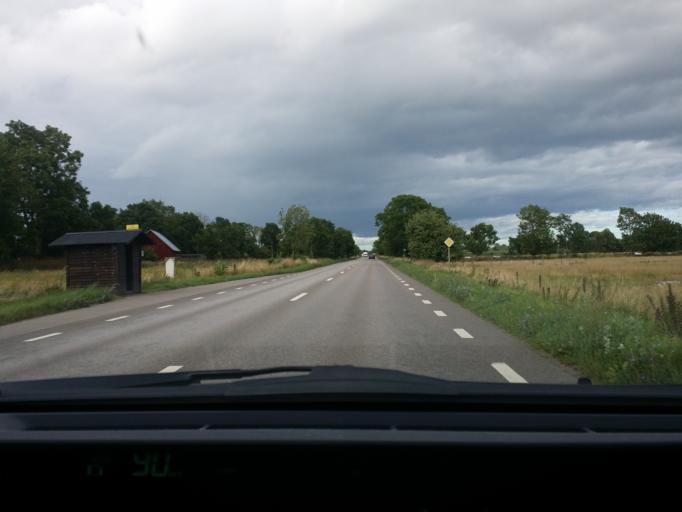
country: SE
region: Kalmar
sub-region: Borgholms Kommun
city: Borgholm
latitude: 56.9172
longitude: 16.7497
